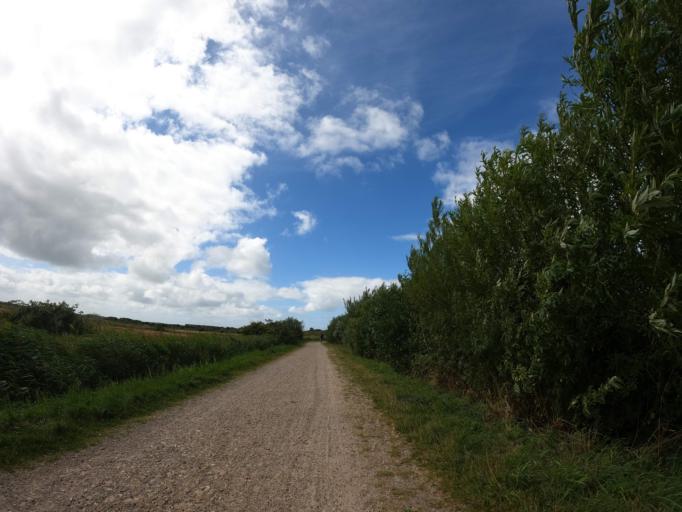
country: DE
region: Schleswig-Holstein
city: Tinnum
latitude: 54.8955
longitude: 8.3245
